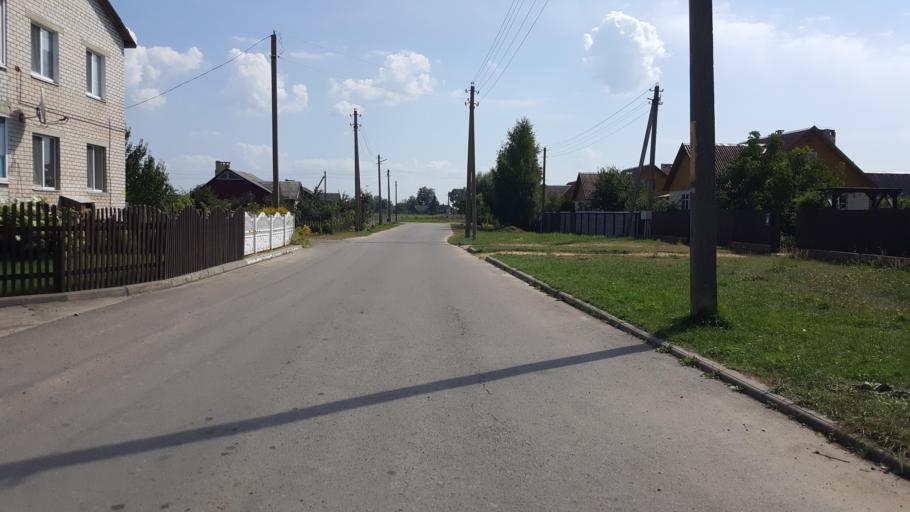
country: PL
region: Podlasie
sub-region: Powiat hajnowski
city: Czeremcha
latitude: 52.4968
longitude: 23.5706
